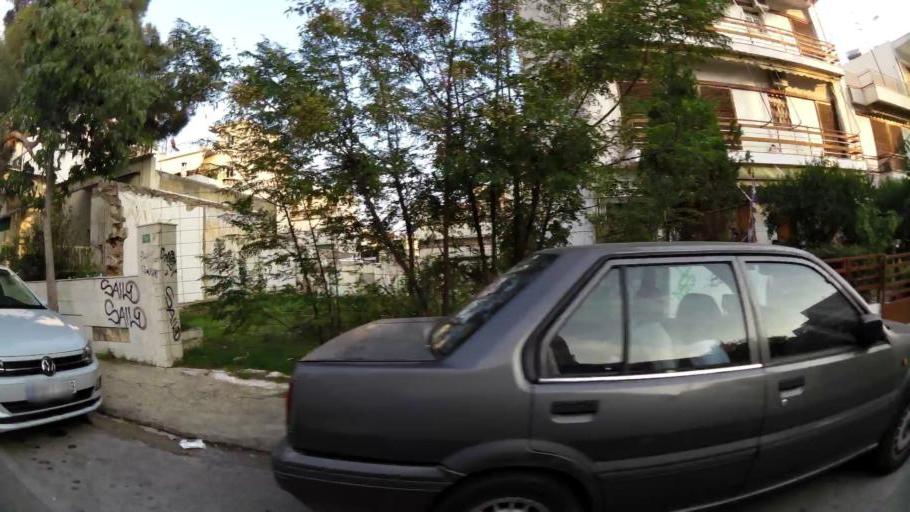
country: GR
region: Attica
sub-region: Nomarchia Athinas
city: Petroupolis
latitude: 38.0385
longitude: 23.6871
